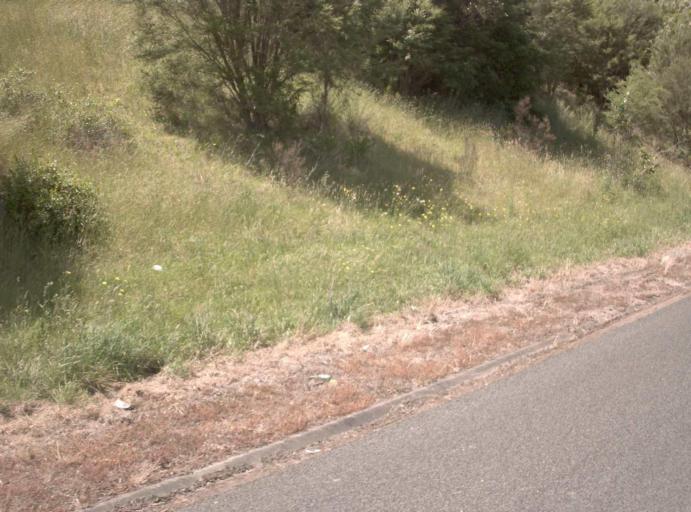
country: AU
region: Victoria
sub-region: Baw Baw
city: Warragul
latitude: -38.1180
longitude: 145.8667
